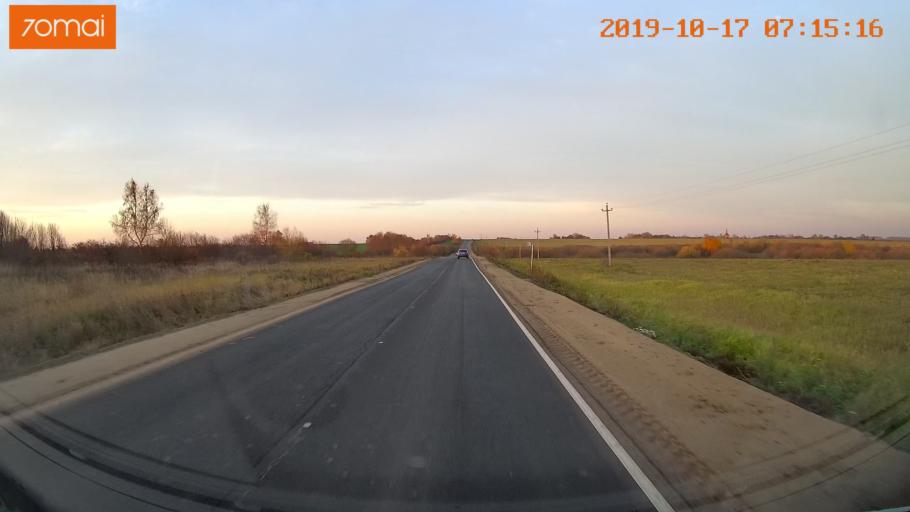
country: RU
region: Vladimir
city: Suzdal'
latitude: 56.3826
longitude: 40.2710
